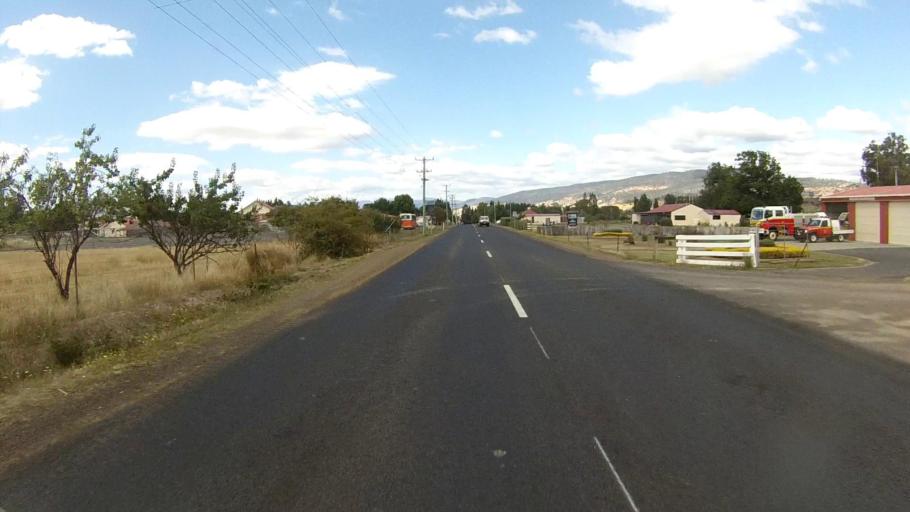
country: AU
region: Tasmania
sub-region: Derwent Valley
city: New Norfolk
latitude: -42.6952
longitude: 146.8877
